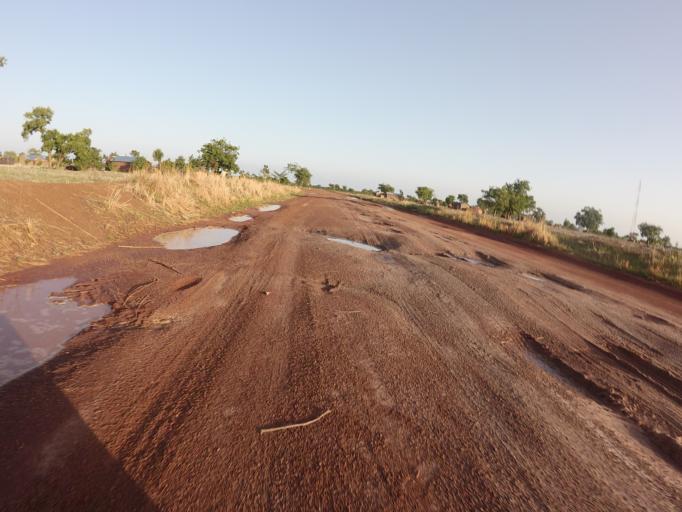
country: TG
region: Savanes
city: Sansanne-Mango
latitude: 10.2961
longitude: -0.0885
